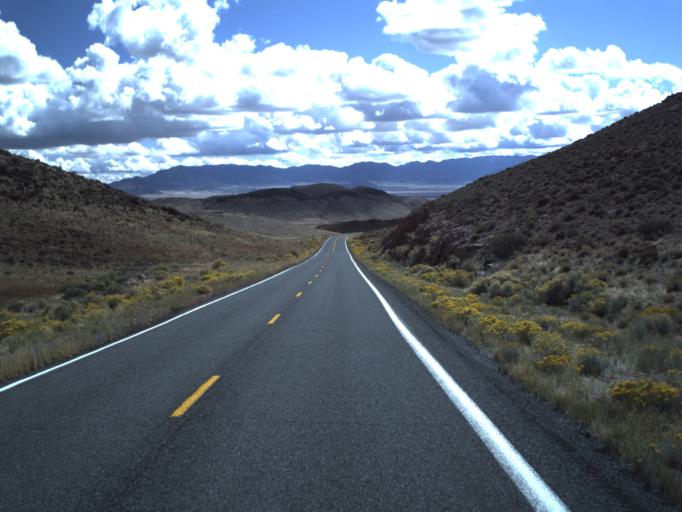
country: US
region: Utah
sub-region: Beaver County
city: Milford
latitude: 38.6145
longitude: -113.8407
